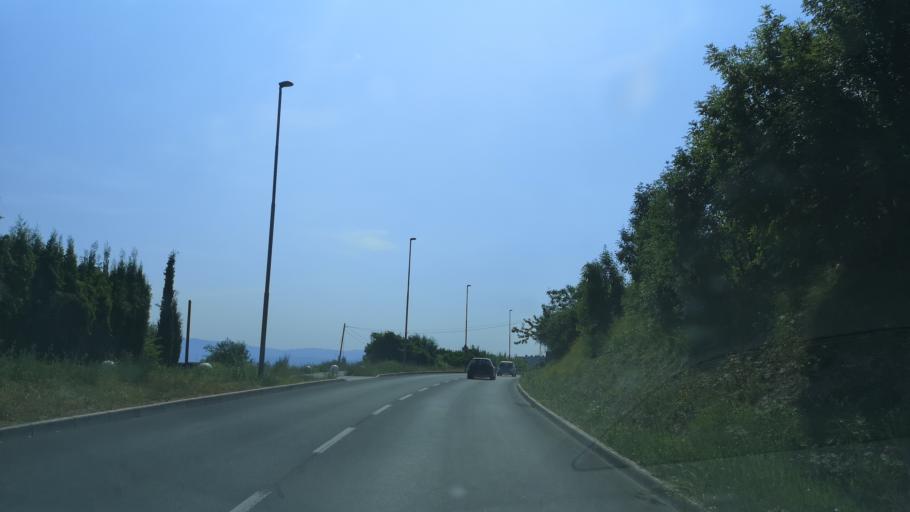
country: SI
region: Koper-Capodistria
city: Koper
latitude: 45.5427
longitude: 13.6957
